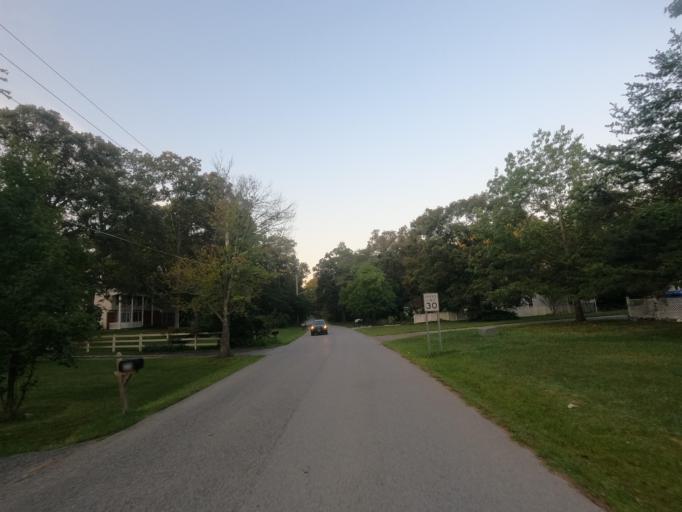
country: US
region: Maryland
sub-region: Prince George's County
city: Accokeek
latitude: 38.6652
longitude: -77.0061
